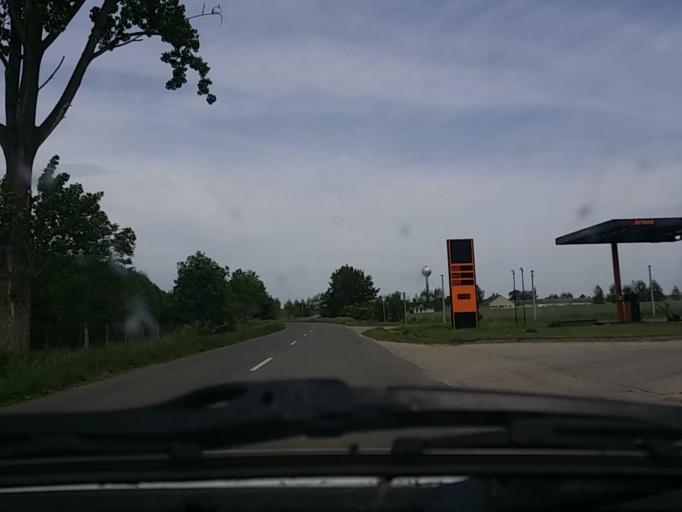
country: HU
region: Baranya
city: Sellye
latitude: 45.8757
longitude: 17.8667
